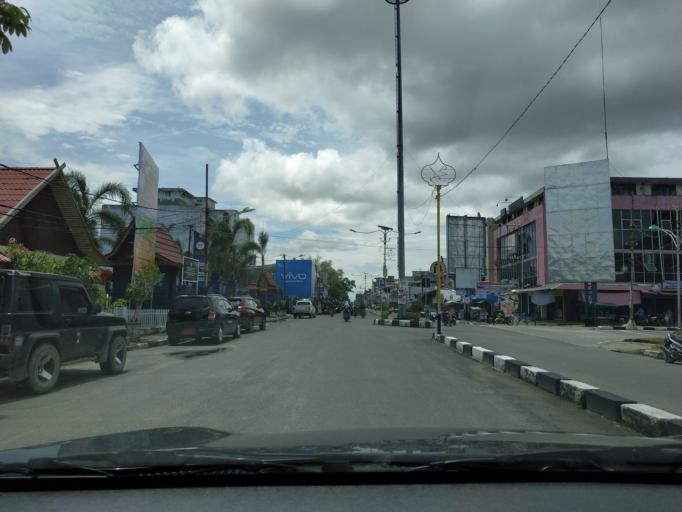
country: ID
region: Riau
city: Tembilahan
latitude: -0.3267
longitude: 103.1598
